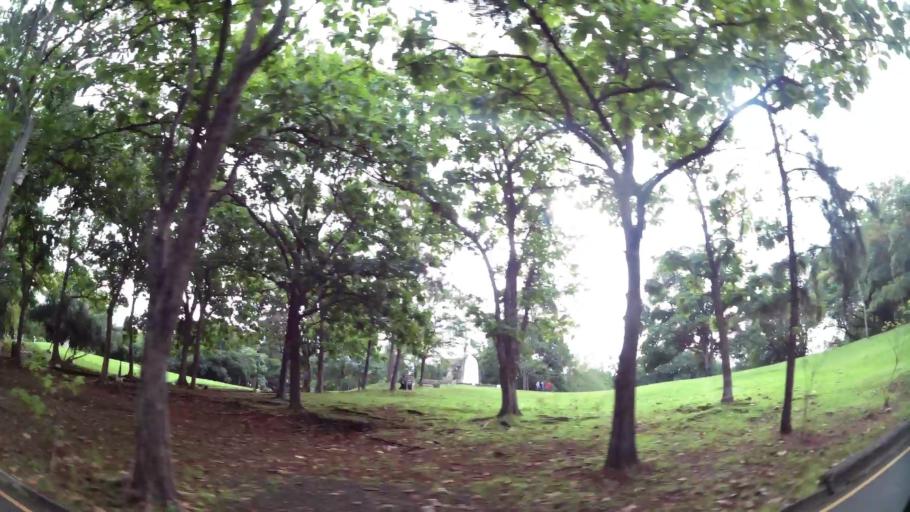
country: PA
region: Panama
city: Panama
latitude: 8.9991
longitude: -79.5076
